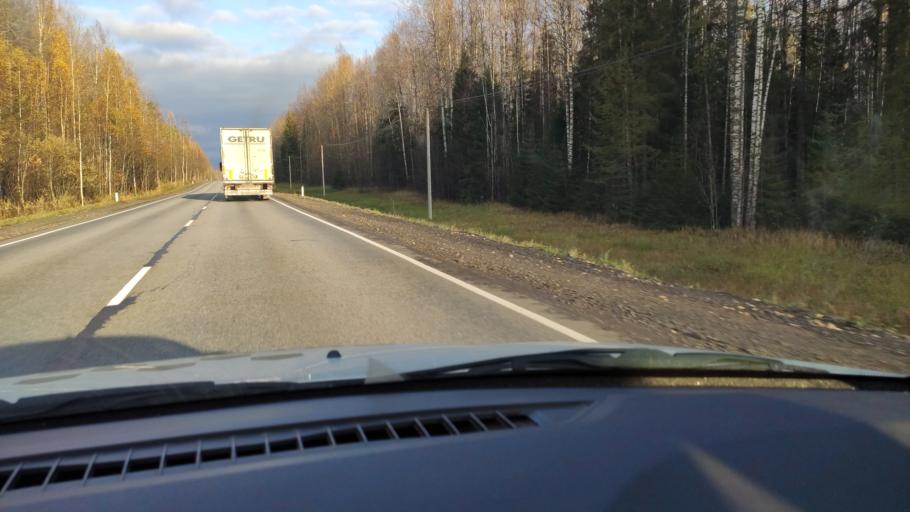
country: RU
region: Kirov
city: Belaya Kholunitsa
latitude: 58.9173
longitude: 51.0956
